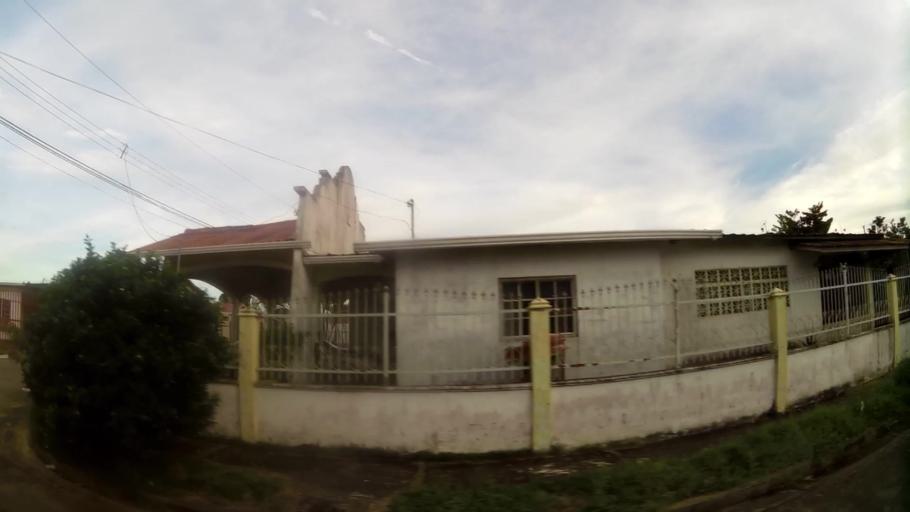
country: PA
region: Panama
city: La Chorrera
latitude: 8.8703
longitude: -79.7677
